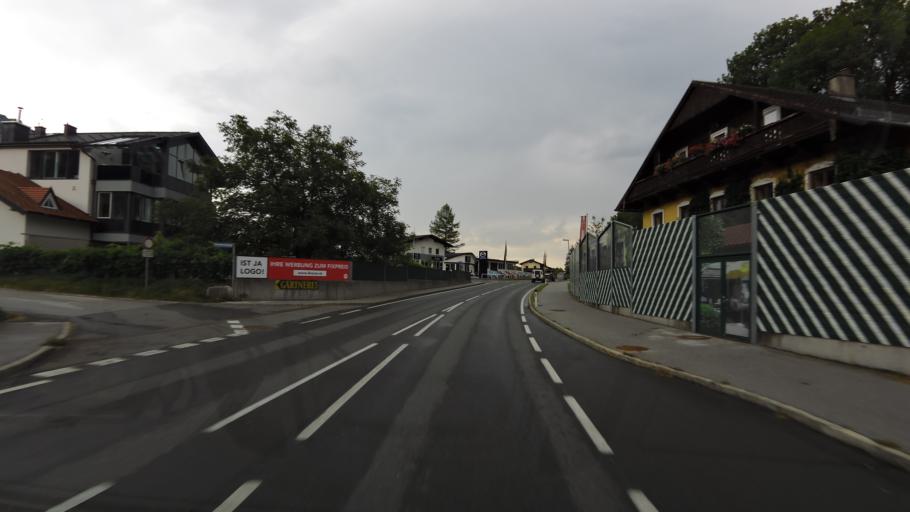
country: DE
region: Bavaria
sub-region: Upper Bavaria
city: Marktschellenberg
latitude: 47.7165
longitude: 13.0614
